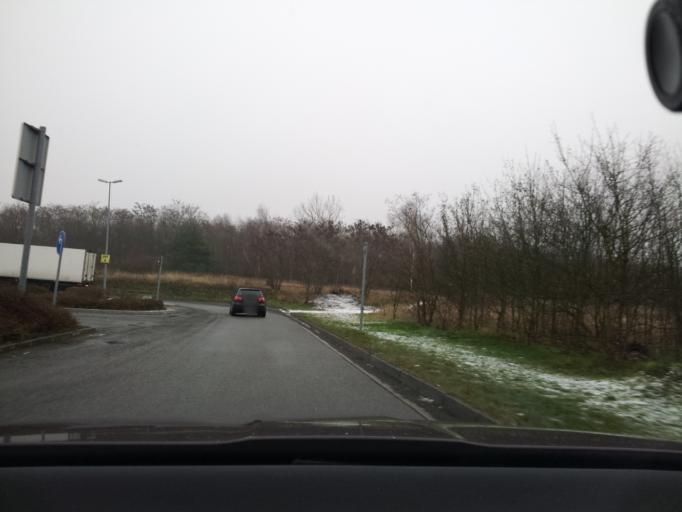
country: DE
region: Brandenburg
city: Wildau
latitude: 52.3120
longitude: 13.6122
